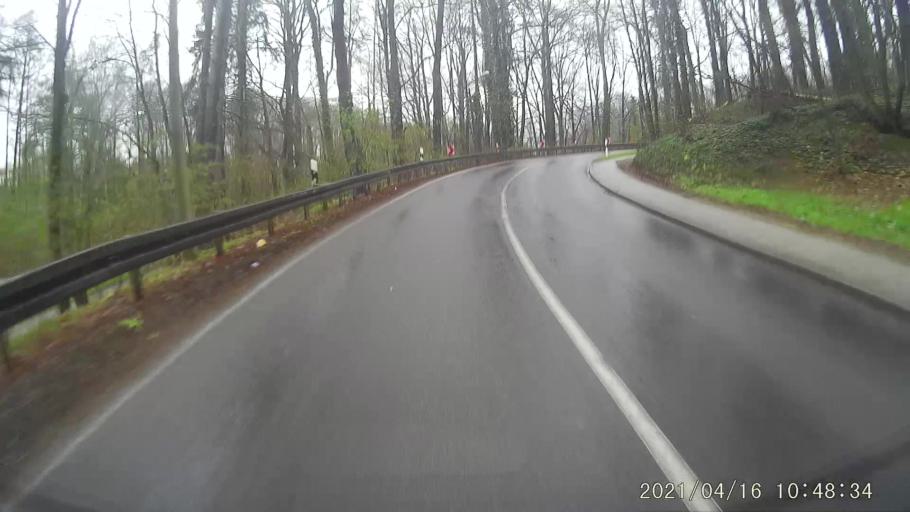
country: DE
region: Saxony
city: Goerlitz
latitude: 51.1335
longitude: 14.9580
